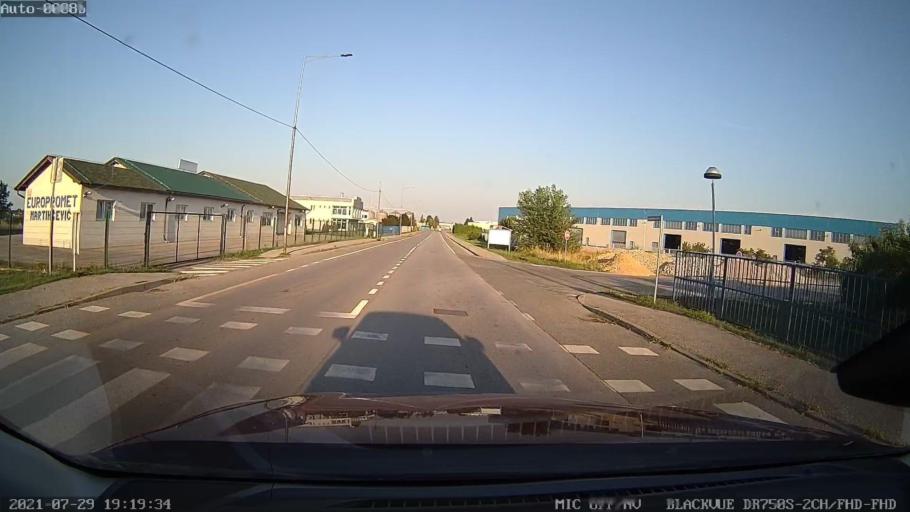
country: HR
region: Varazdinska
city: Ludbreg
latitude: 46.2573
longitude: 16.5997
